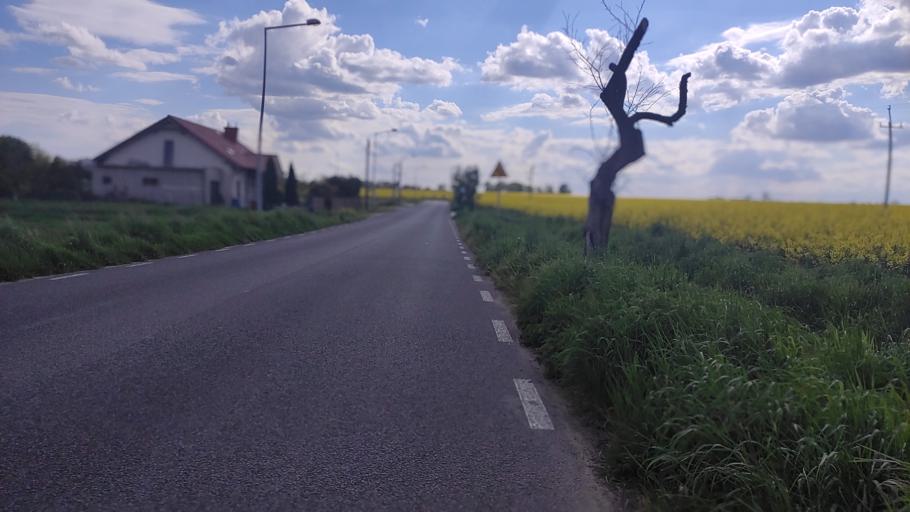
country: PL
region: Greater Poland Voivodeship
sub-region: Powiat poznanski
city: Kostrzyn
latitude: 52.4100
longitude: 17.1688
